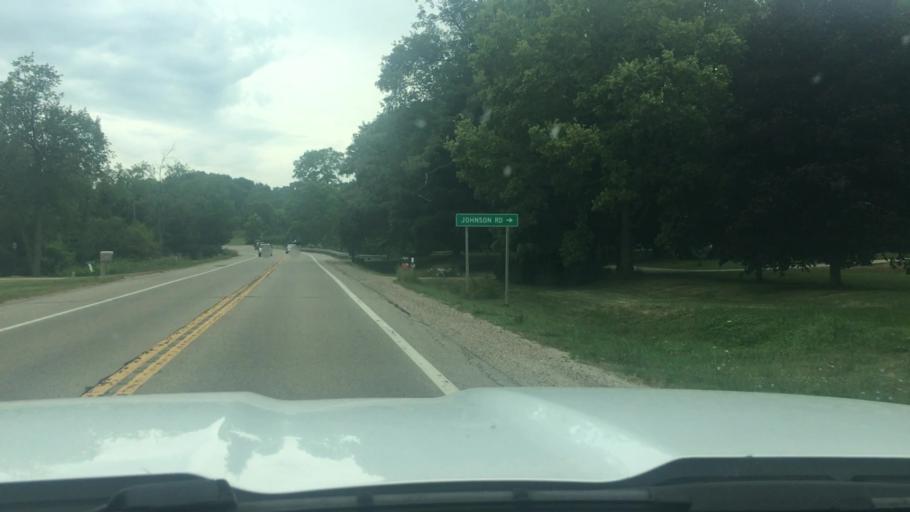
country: US
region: Michigan
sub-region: Ionia County
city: Saranac
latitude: 42.9568
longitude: -85.1708
